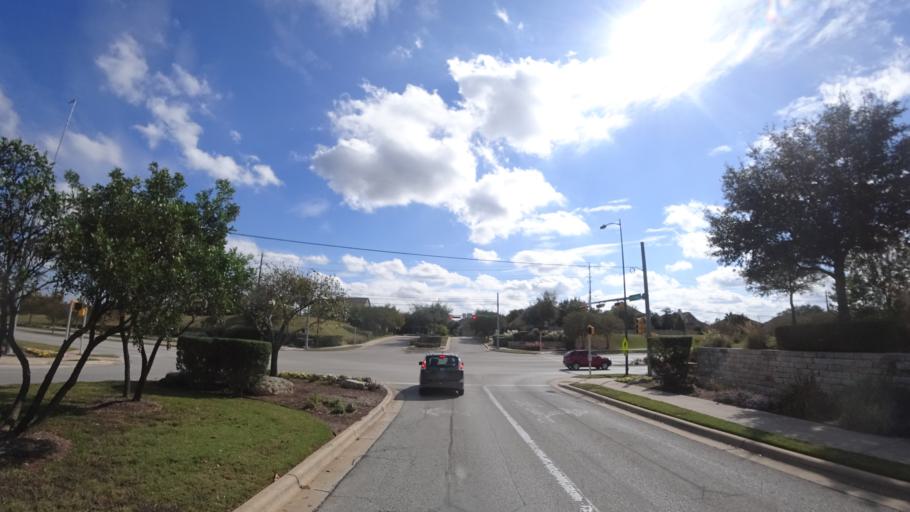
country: US
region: Texas
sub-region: Travis County
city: Hudson Bend
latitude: 30.3626
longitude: -97.9002
